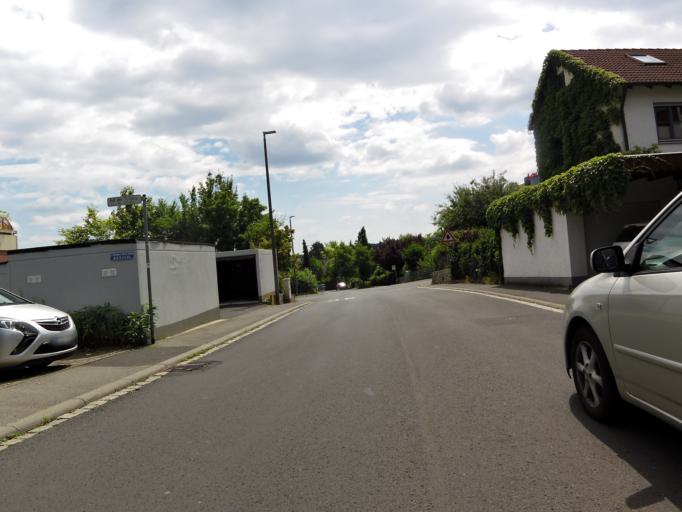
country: DE
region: Bavaria
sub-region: Regierungsbezirk Unterfranken
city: Wuerzburg
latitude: 49.8049
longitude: 9.9716
